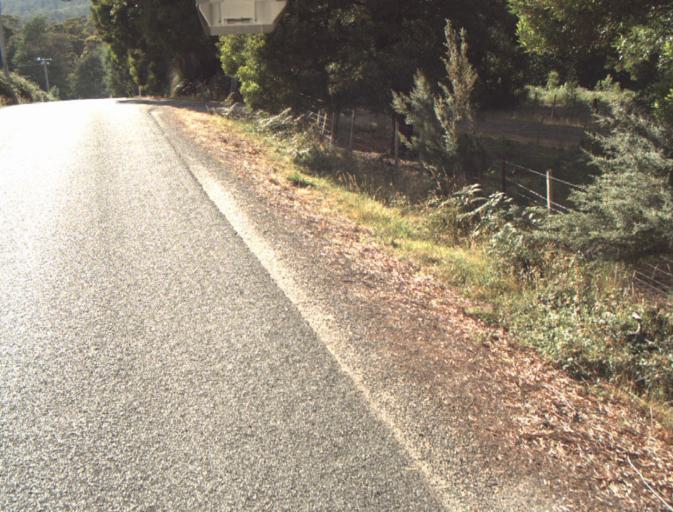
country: AU
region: Tasmania
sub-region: Launceston
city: Mayfield
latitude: -41.2855
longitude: 147.2018
